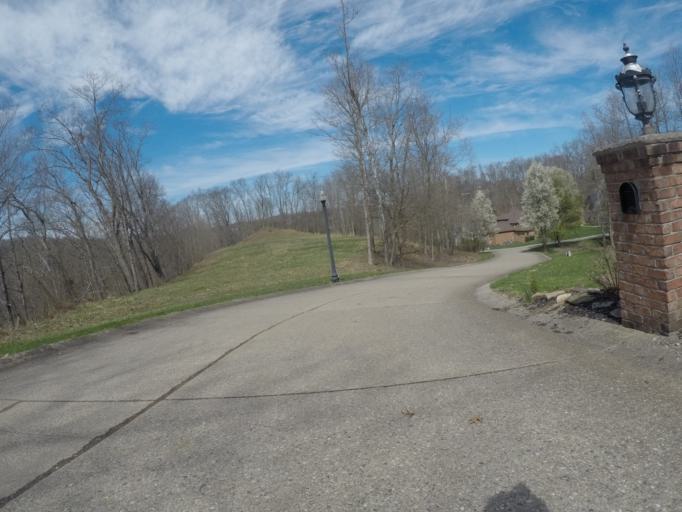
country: US
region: West Virginia
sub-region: Cabell County
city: Pea Ridge
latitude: 38.4034
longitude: -82.3122
